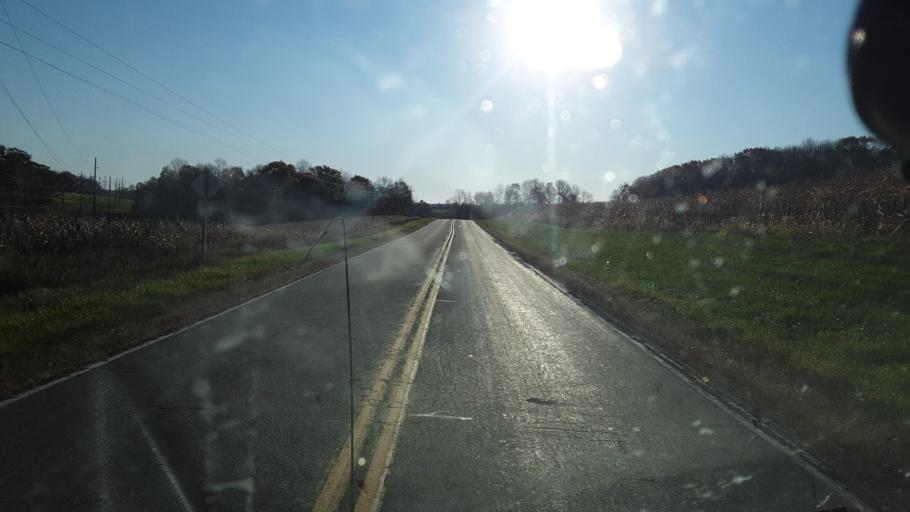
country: US
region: Wisconsin
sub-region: Vernon County
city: Hillsboro
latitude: 43.6673
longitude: -90.4568
